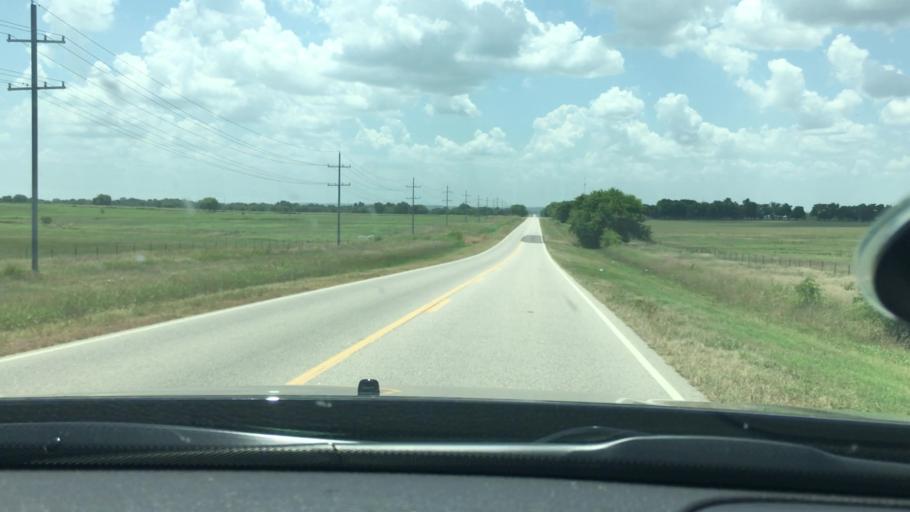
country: US
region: Oklahoma
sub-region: Pontotoc County
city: Ada
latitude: 34.6711
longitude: -96.6349
